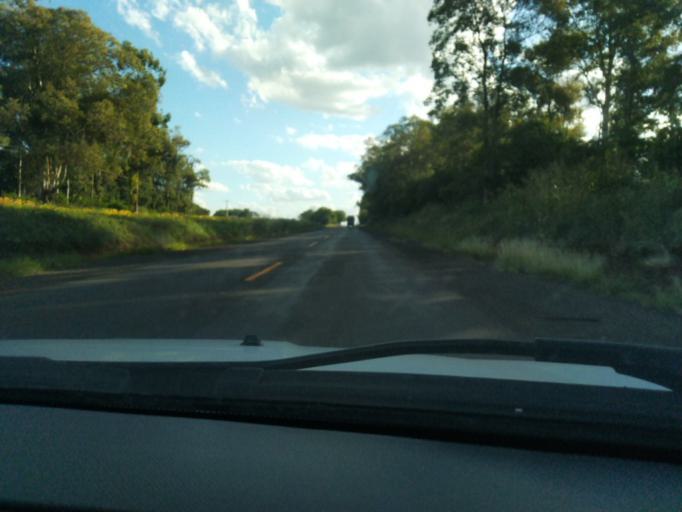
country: AR
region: Corrientes
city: Garruchos
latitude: -28.5494
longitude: -55.5641
